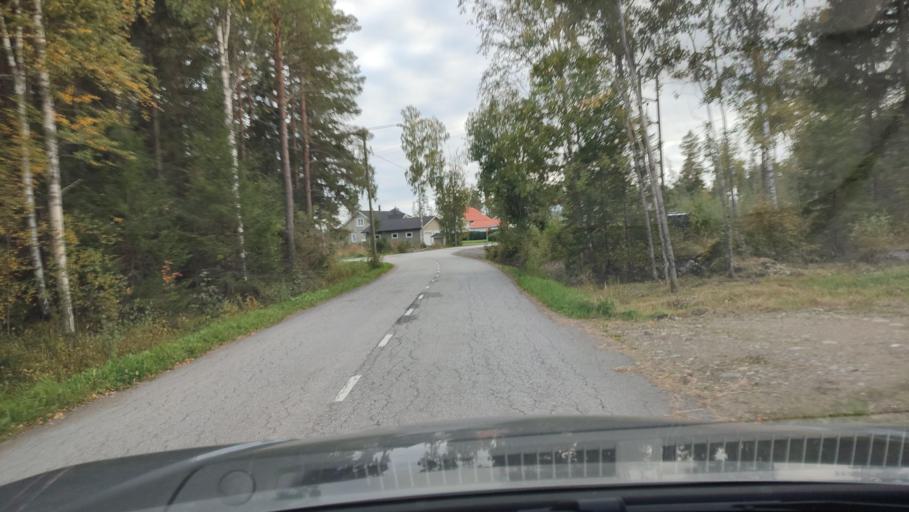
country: FI
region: Ostrobothnia
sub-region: Sydosterbotten
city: Kristinestad
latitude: 62.2573
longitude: 21.3841
